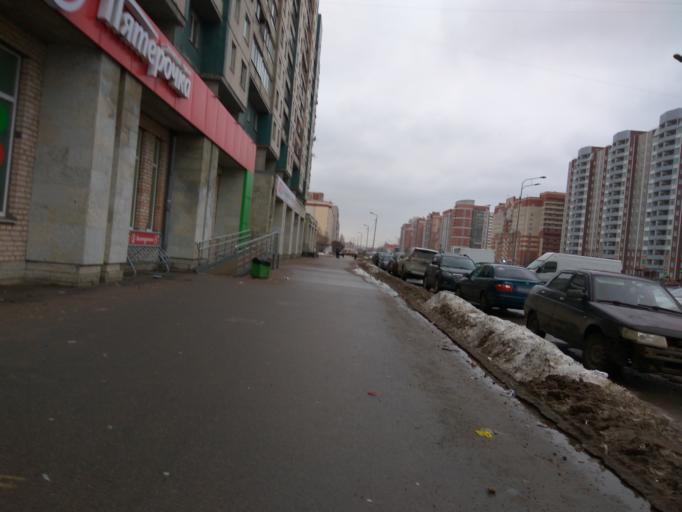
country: RU
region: St.-Petersburg
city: Staraya Derevnya
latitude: 60.0039
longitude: 30.2379
